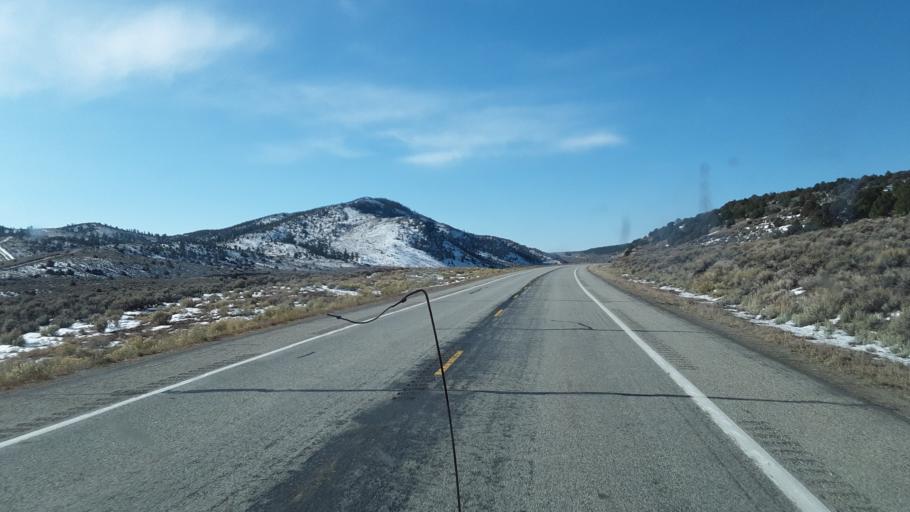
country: US
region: Colorado
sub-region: Costilla County
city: San Luis
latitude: 37.5089
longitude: -105.3176
